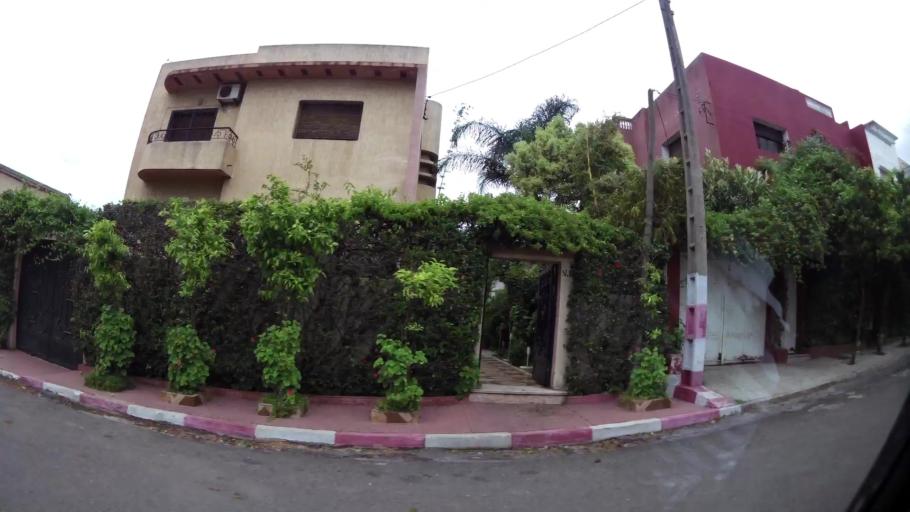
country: MA
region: Grand Casablanca
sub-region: Mediouna
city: Tit Mellil
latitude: 33.5659
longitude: -7.5333
